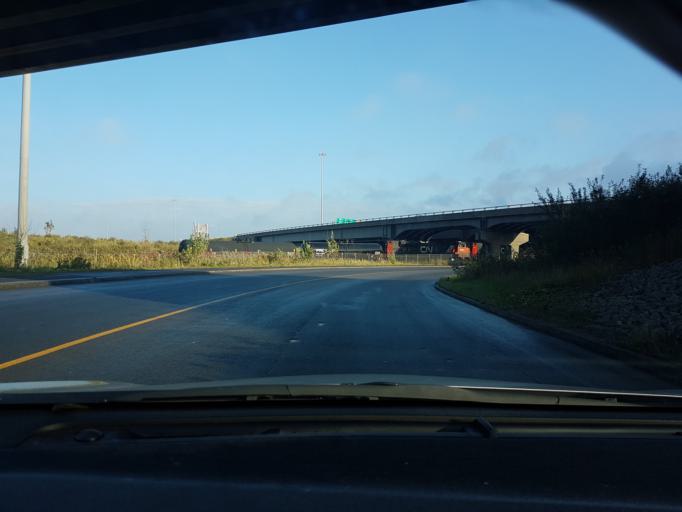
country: CA
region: Quebec
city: L'Ancienne-Lorette
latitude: 46.7951
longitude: -71.2900
